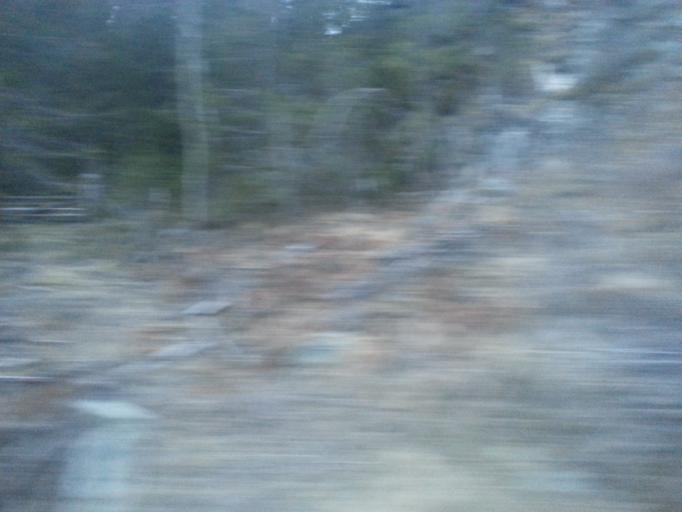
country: NO
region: Sor-Trondelag
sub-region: Rennebu
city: Berkak
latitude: 62.7677
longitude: 9.9910
